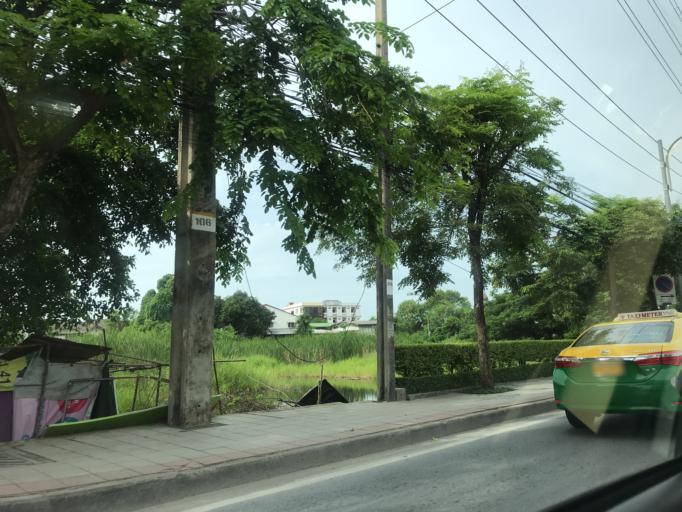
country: TH
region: Bangkok
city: Bueng Kum
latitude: 13.7849
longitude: 100.6748
